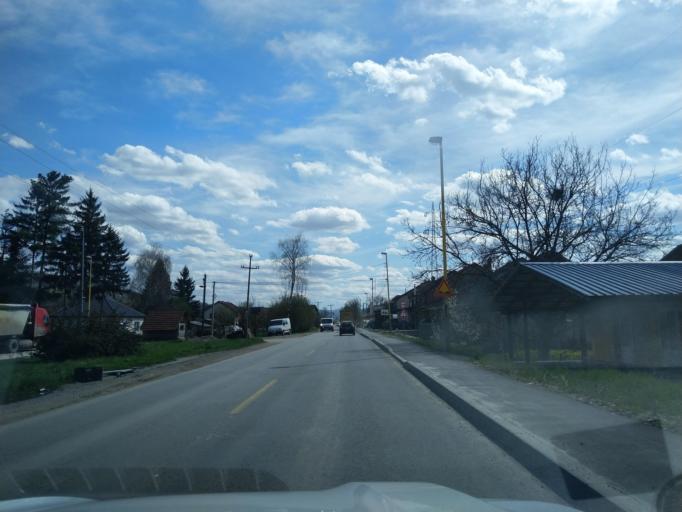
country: RS
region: Central Serbia
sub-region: Zlatiborski Okrug
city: Arilje
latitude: 43.7502
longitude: 20.1051
